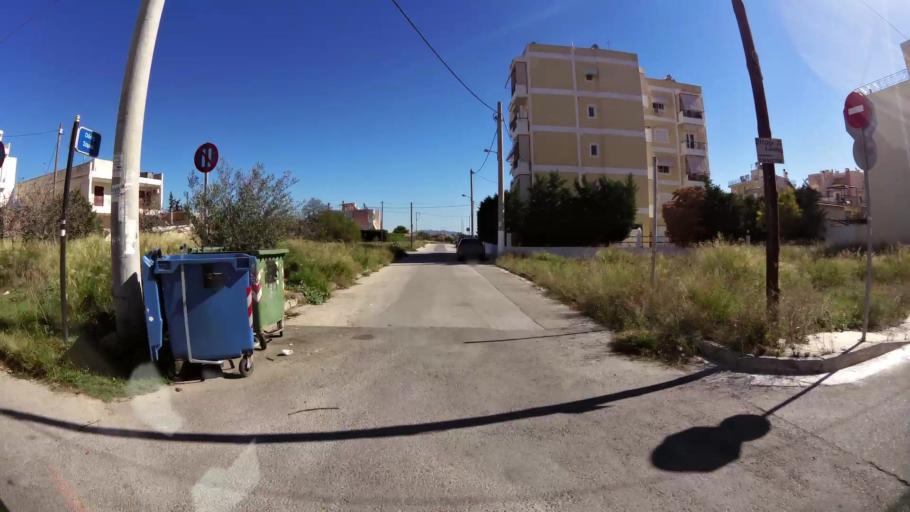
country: GR
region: Attica
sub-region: Nomarchia Anatolikis Attikis
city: Koropi
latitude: 37.9117
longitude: 23.8780
